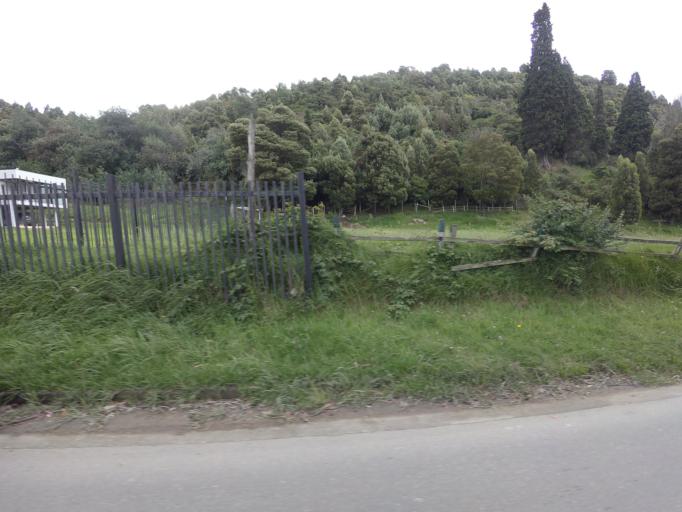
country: CO
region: Cundinamarca
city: Cajica
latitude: 4.9447
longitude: -74.0259
